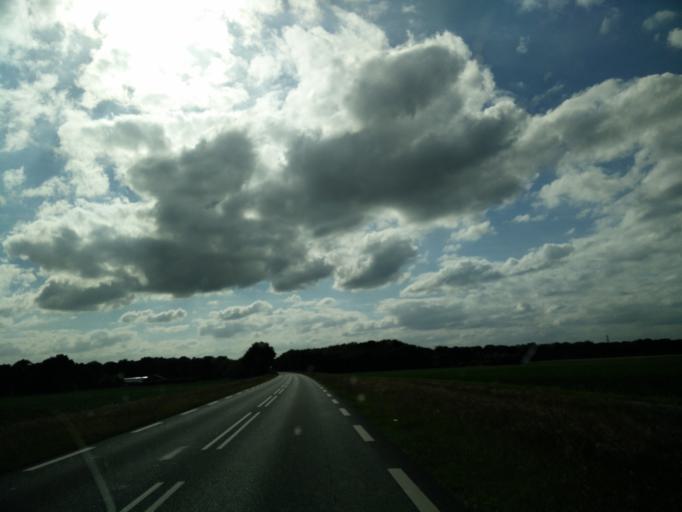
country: NL
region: Drenthe
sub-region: Gemeente Emmen
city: Emmen
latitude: 52.7897
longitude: 6.8728
